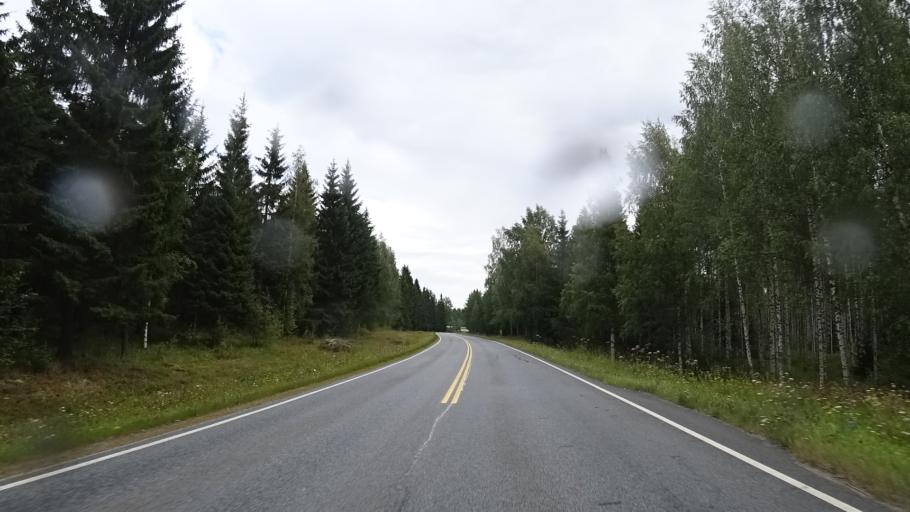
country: FI
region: North Karelia
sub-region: Keski-Karjala
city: Kesaelahti
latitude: 62.1100
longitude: 29.7512
